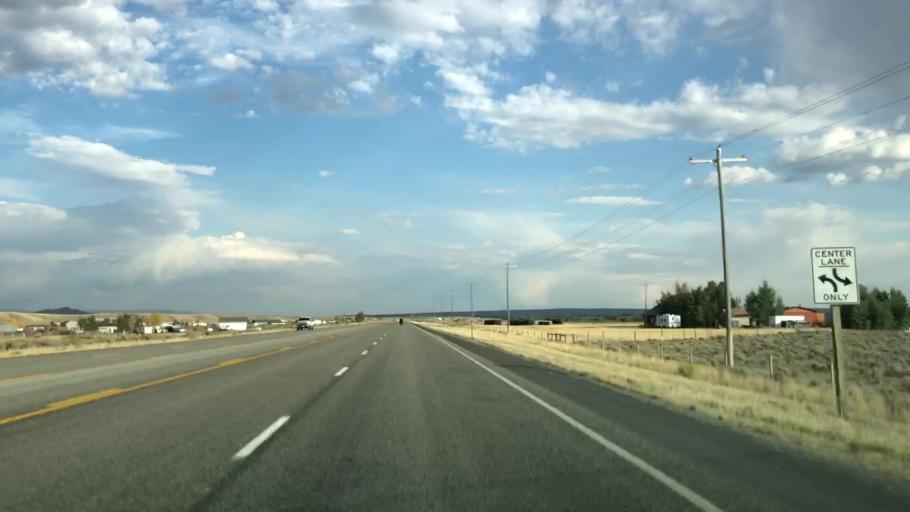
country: US
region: Wyoming
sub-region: Sublette County
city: Pinedale
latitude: 42.7779
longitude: -109.7602
